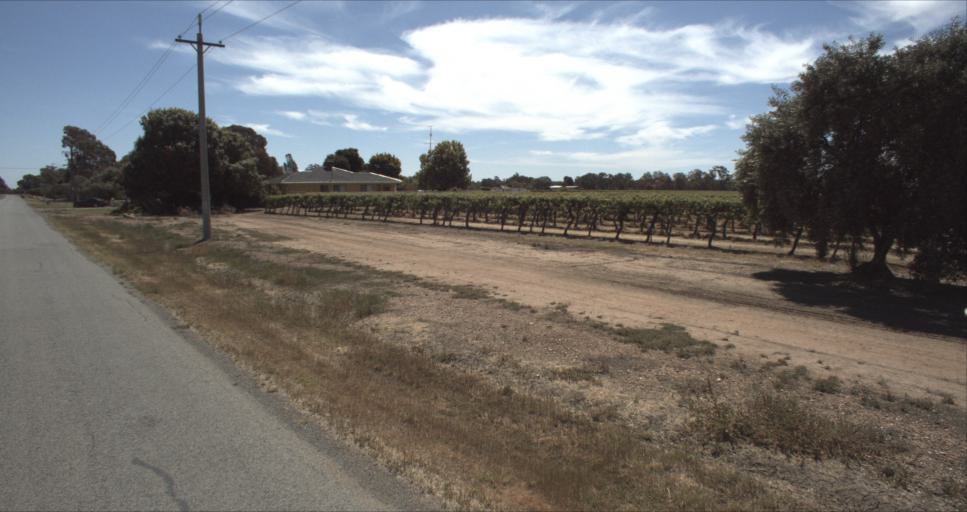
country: AU
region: New South Wales
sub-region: Leeton
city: Leeton
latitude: -34.5723
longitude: 146.4188
